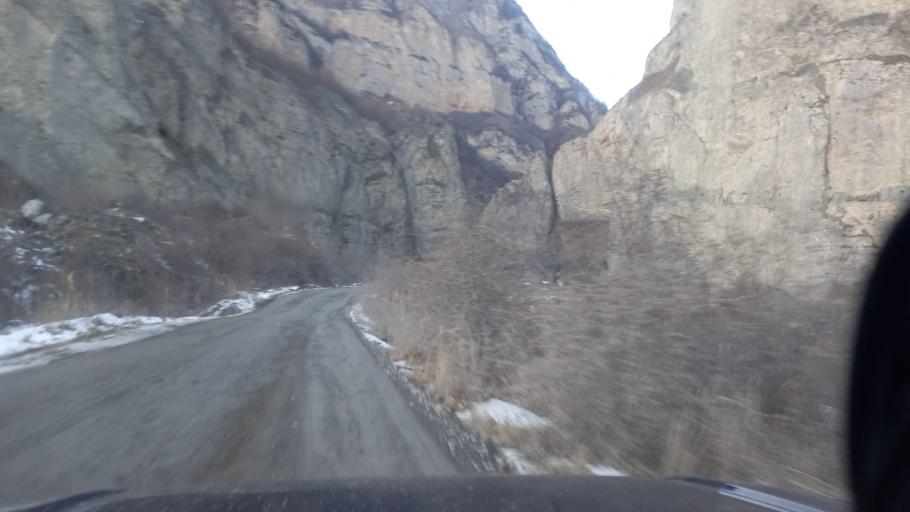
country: RU
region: Ingushetiya
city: Dzhayrakh
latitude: 42.8621
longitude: 44.5200
